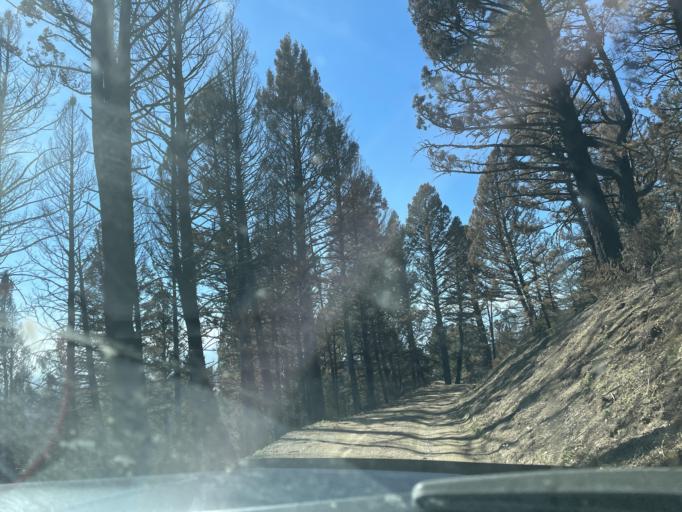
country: US
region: Montana
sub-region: Broadwater County
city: Townsend
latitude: 46.5066
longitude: -111.2823
